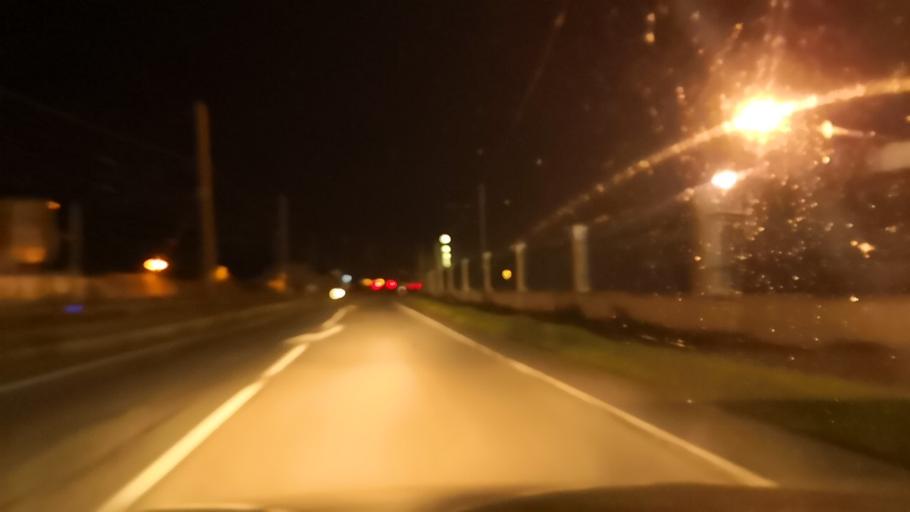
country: PT
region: Setubal
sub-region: Setubal
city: Setubal
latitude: 38.5185
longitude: -8.8758
